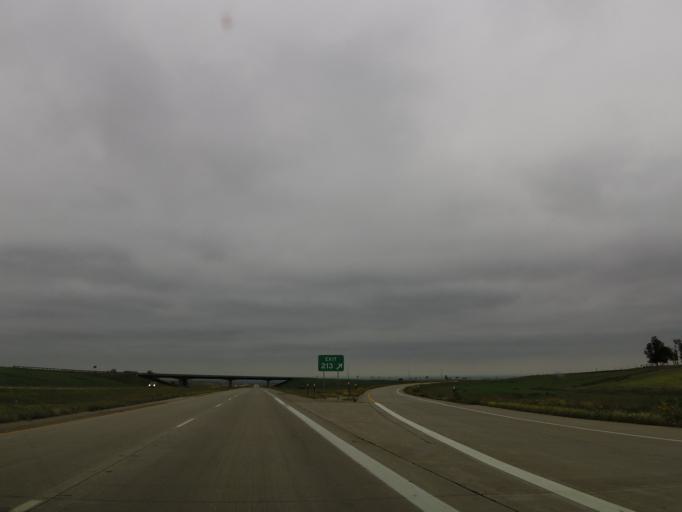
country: US
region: South Dakota
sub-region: Roberts County
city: Sisseton
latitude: 45.4005
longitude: -97.0228
